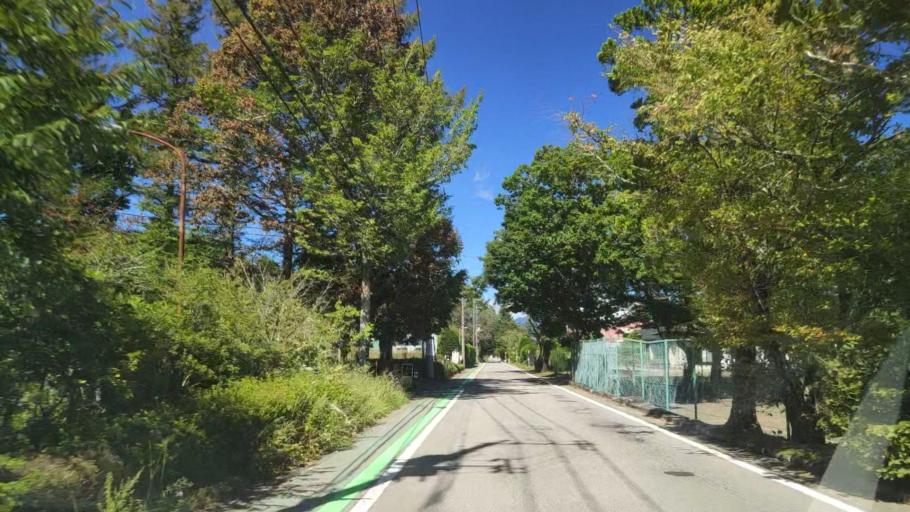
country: JP
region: Shizuoka
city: Gotemba
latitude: 35.4119
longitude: 138.8552
